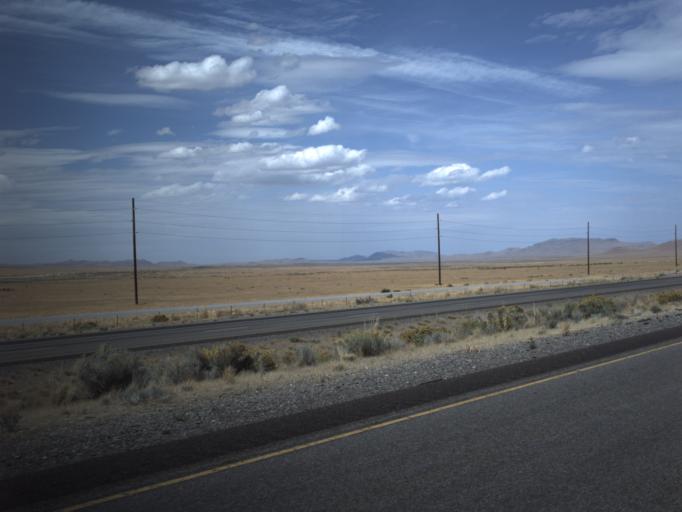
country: US
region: Utah
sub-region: Tooele County
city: Grantsville
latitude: 40.7875
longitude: -112.9589
